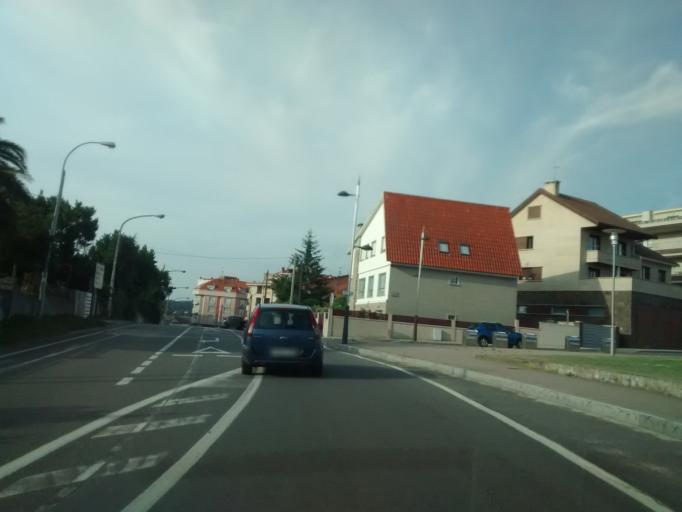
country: ES
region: Galicia
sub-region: Provincia de Pontevedra
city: Sanxenxo
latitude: 42.3923
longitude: -8.8297
